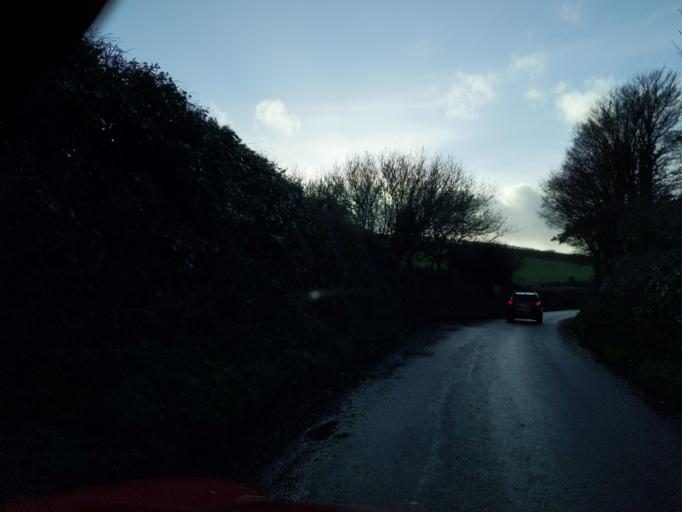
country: GB
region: England
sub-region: Cornwall
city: Fowey
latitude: 50.3335
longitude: -4.5965
